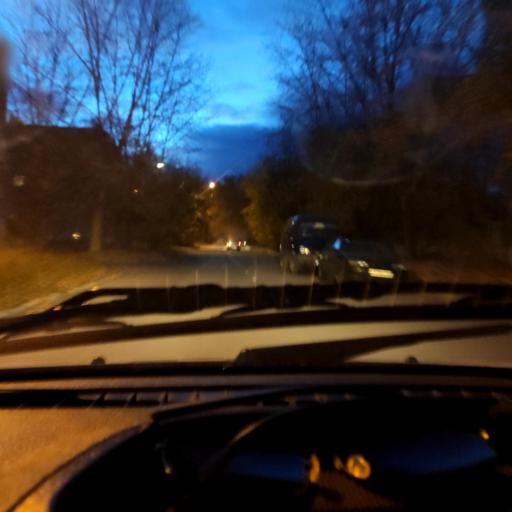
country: RU
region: Samara
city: Zhigulevsk
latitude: 53.4662
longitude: 49.5271
